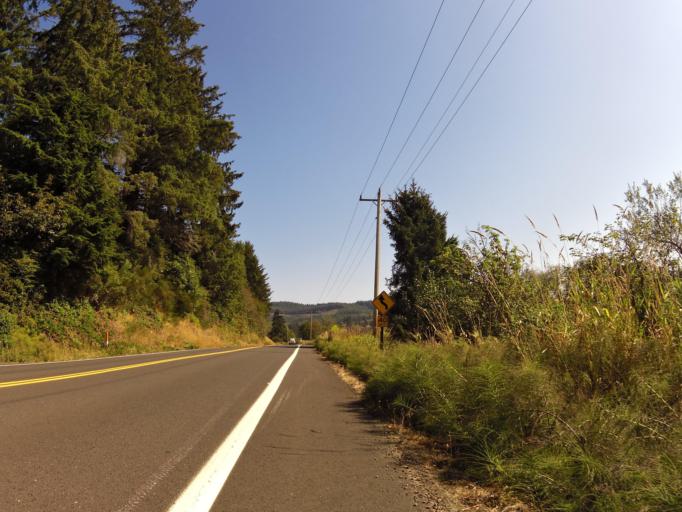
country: US
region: Oregon
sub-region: Tillamook County
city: Pacific City
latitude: 45.1803
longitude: -123.9352
